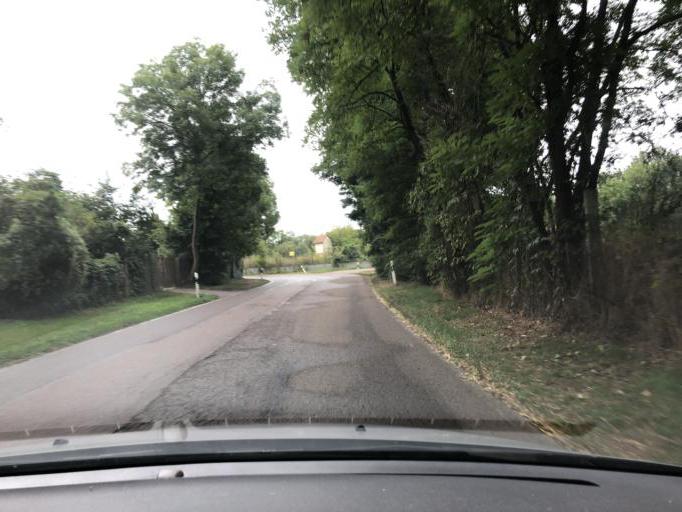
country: DE
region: Saxony-Anhalt
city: Nienburg/Saale
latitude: 51.8452
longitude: 11.7768
